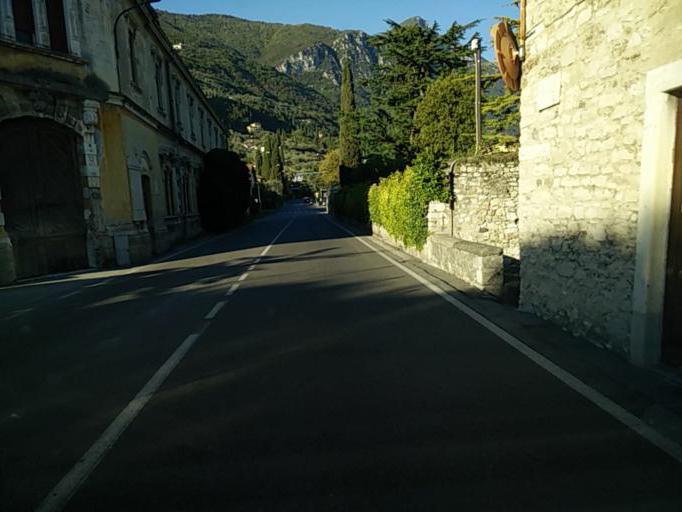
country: IT
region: Lombardy
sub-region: Provincia di Brescia
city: Gargnano
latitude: 45.6789
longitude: 10.6538
